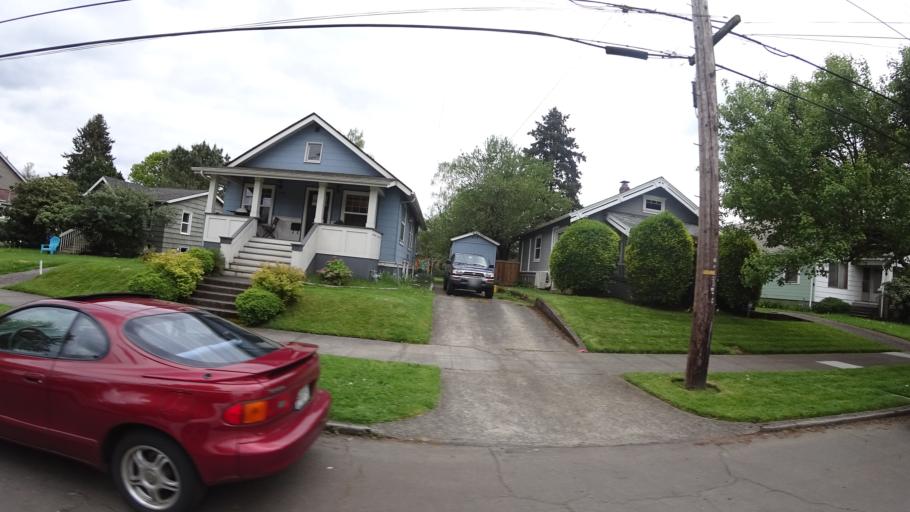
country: US
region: Oregon
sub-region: Clackamas County
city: Milwaukie
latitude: 45.4831
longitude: -122.6468
